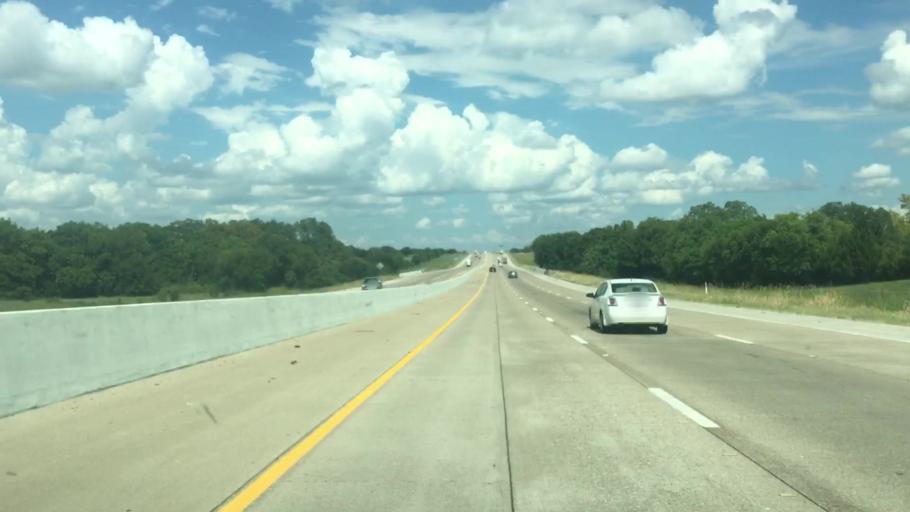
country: US
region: Texas
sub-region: Ellis County
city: Plum Grove
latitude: 32.1200
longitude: -96.9811
